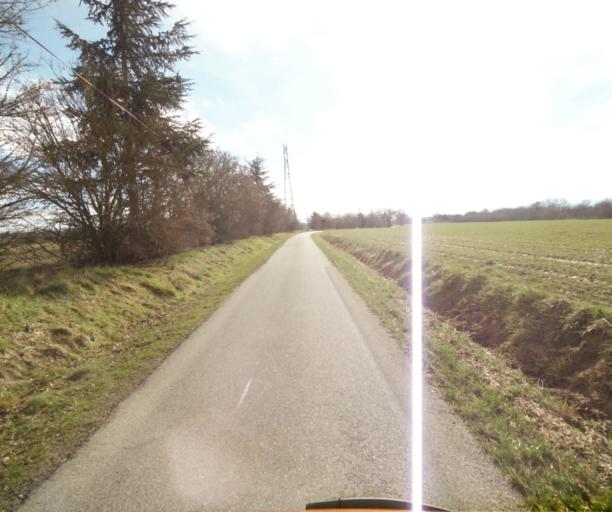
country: FR
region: Midi-Pyrenees
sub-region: Departement de l'Ariege
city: La Tour-du-Crieu
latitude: 43.1262
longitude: 1.6951
